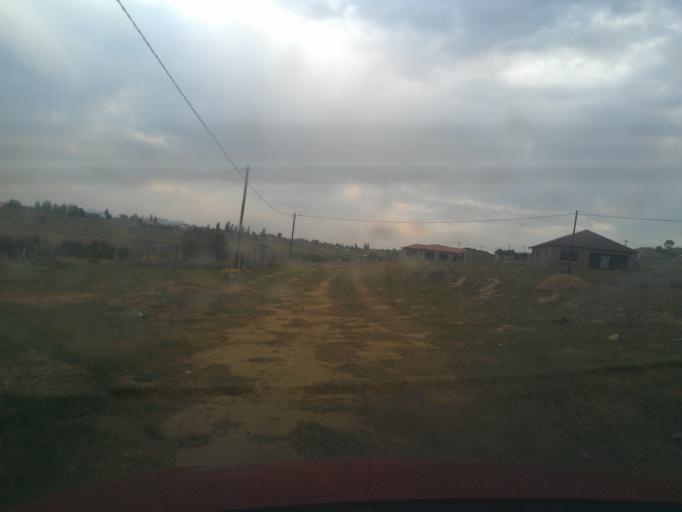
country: LS
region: Berea
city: Teyateyaneng
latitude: -29.1295
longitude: 27.7637
